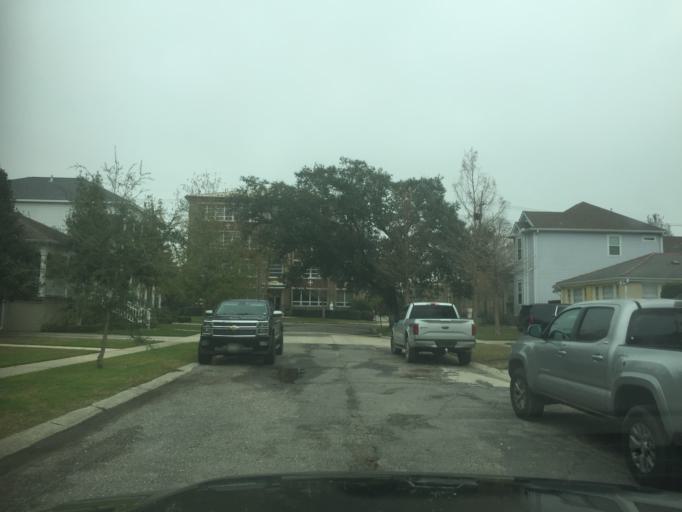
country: US
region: Louisiana
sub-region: Jefferson Parish
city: Metairie
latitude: 30.0174
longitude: -90.1099
